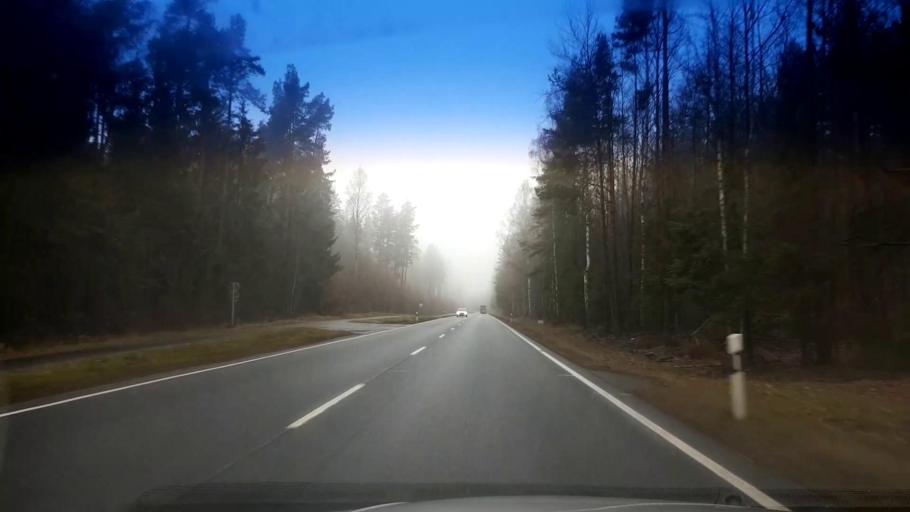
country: DE
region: Bavaria
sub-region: Upper Palatinate
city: Leonberg
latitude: 49.9166
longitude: 12.2940
